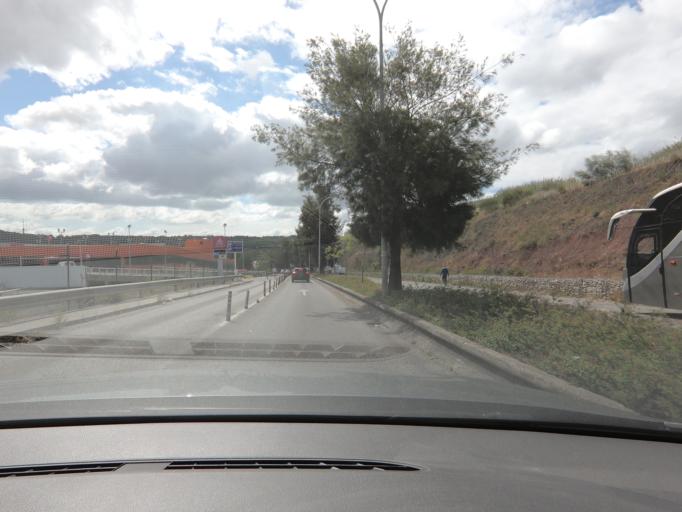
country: PT
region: Lisbon
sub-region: Oeiras
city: Linda-a-Velha
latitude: 38.7272
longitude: -9.2201
